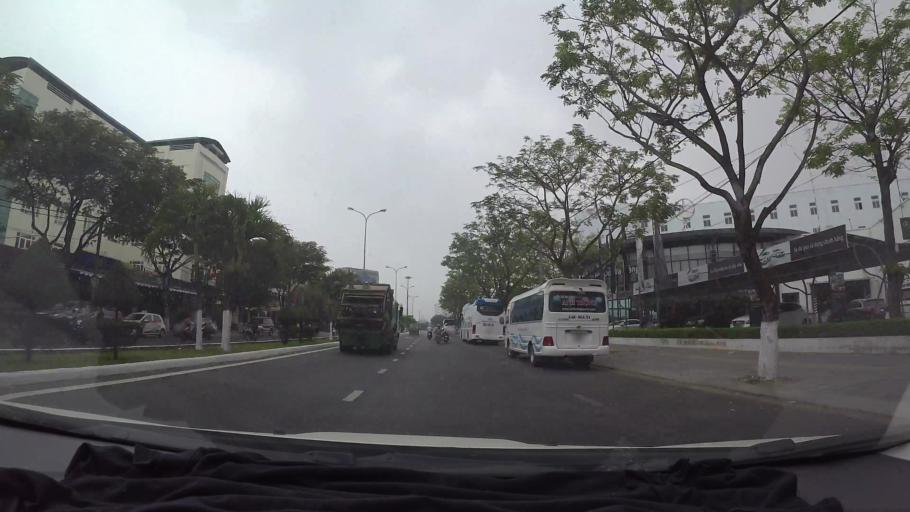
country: VN
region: Da Nang
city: Da Nang
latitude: 16.0488
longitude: 108.2095
